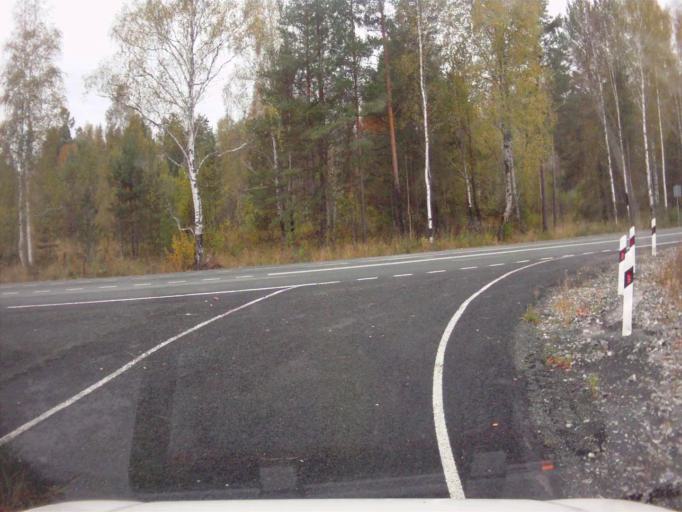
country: RU
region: Chelyabinsk
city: Nyazepetrovsk
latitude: 56.0428
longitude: 59.7766
